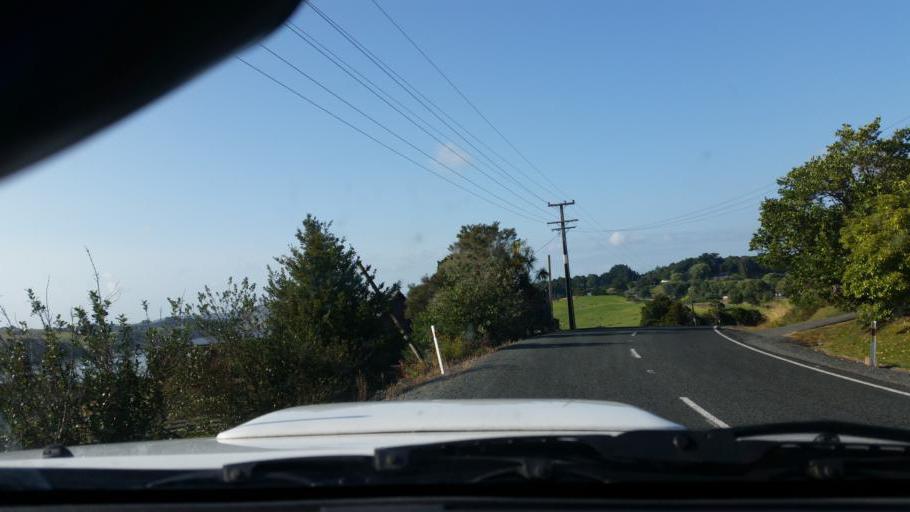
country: NZ
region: Northland
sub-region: Whangarei
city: Ruakaka
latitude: -36.1296
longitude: 174.2300
